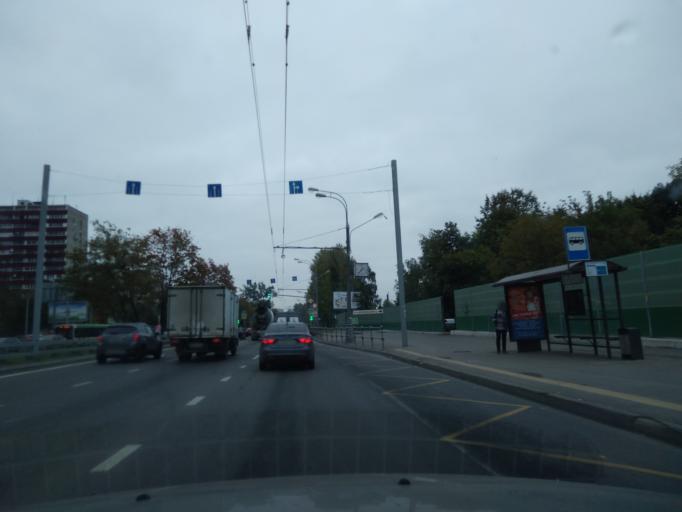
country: RU
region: Moscow
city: Likhobory
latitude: 55.8398
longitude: 37.5481
